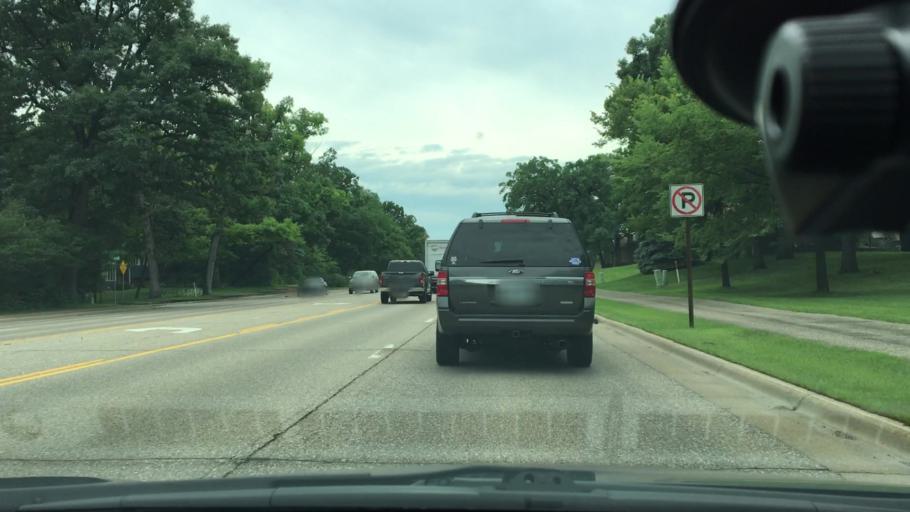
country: US
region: Minnesota
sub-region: Hennepin County
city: Maple Grove
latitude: 45.0760
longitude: -93.4313
